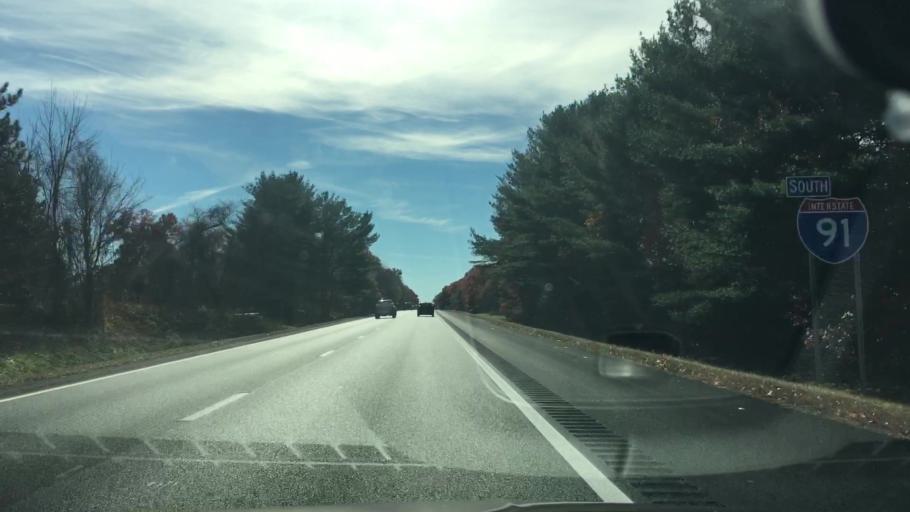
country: US
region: Massachusetts
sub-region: Franklin County
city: Whately
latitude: 42.4300
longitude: -72.6229
